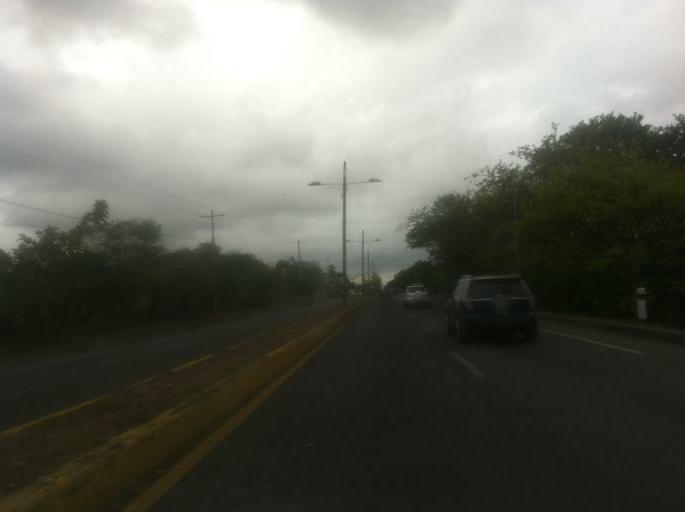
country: NI
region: Masaya
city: Nindiri
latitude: 12.0082
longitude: -86.1377
